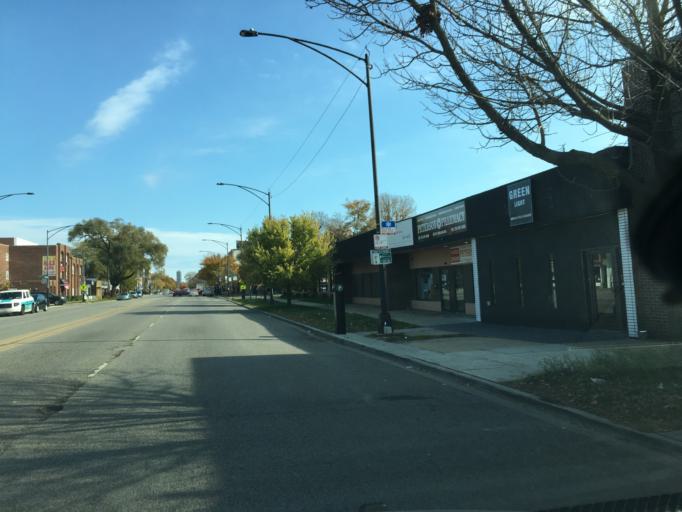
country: US
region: Illinois
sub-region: Cook County
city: Lincolnwood
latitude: 41.9904
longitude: -87.6932
